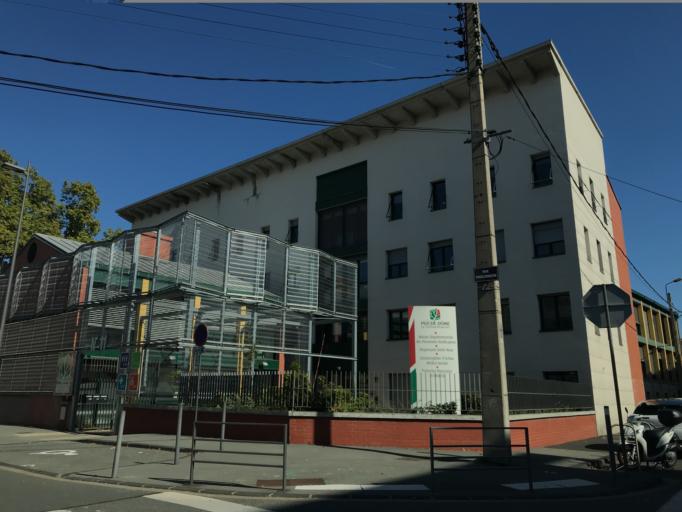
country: FR
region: Auvergne
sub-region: Departement du Puy-de-Dome
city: Clermont-Ferrand
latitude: 45.7865
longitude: 3.1077
